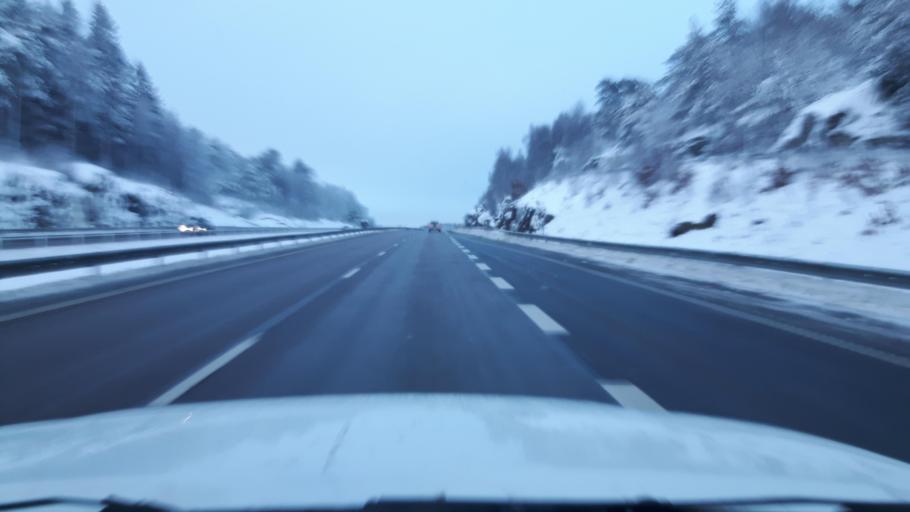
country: SE
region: Halland
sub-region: Kungsbacka Kommun
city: Frillesas
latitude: 57.3323
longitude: 12.2065
